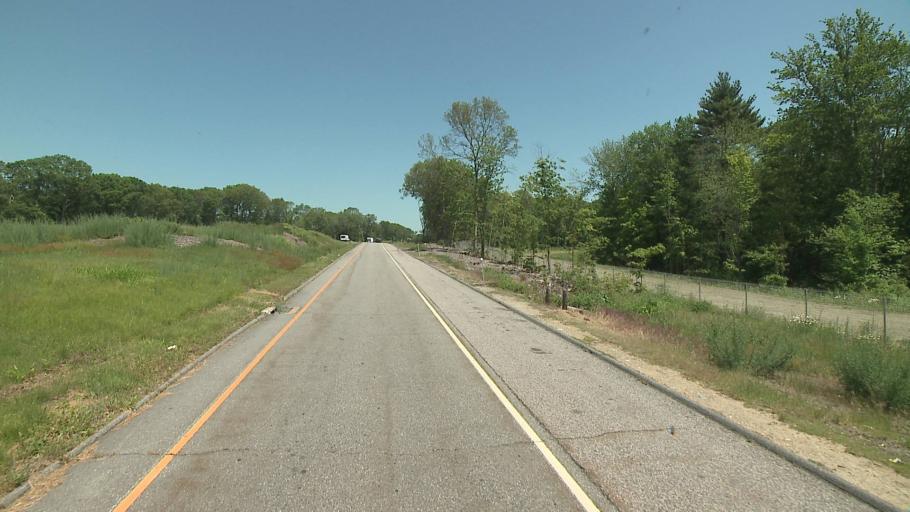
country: US
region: Connecticut
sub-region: New London County
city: Jewett City
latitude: 41.6151
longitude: -71.9451
